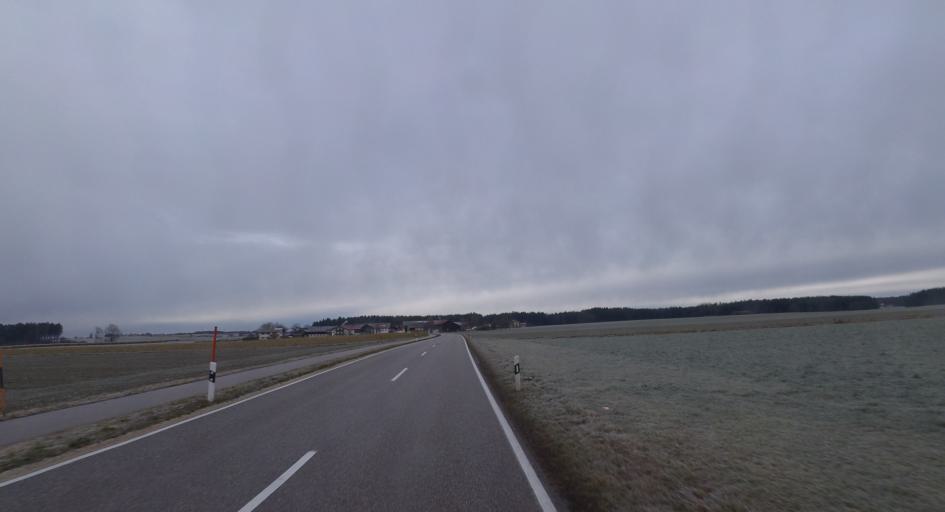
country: DE
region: Bavaria
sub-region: Upper Bavaria
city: Nussdorf
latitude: 47.9370
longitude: 12.6473
